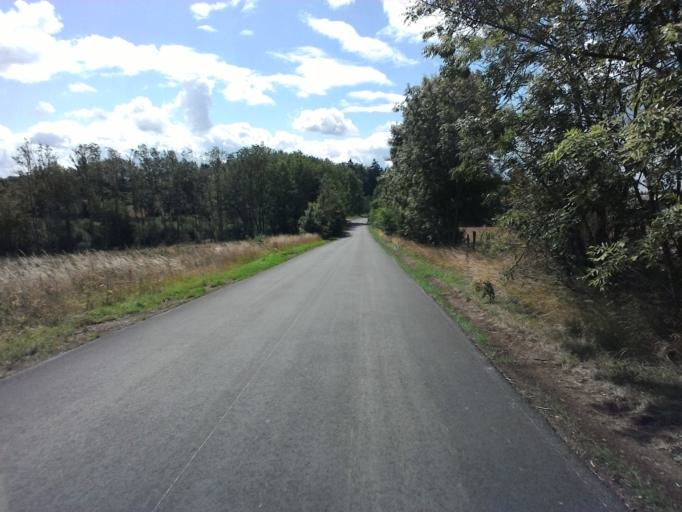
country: BE
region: Wallonia
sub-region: Province du Luxembourg
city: Habay-la-Vieille
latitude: 49.7676
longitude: 5.6232
